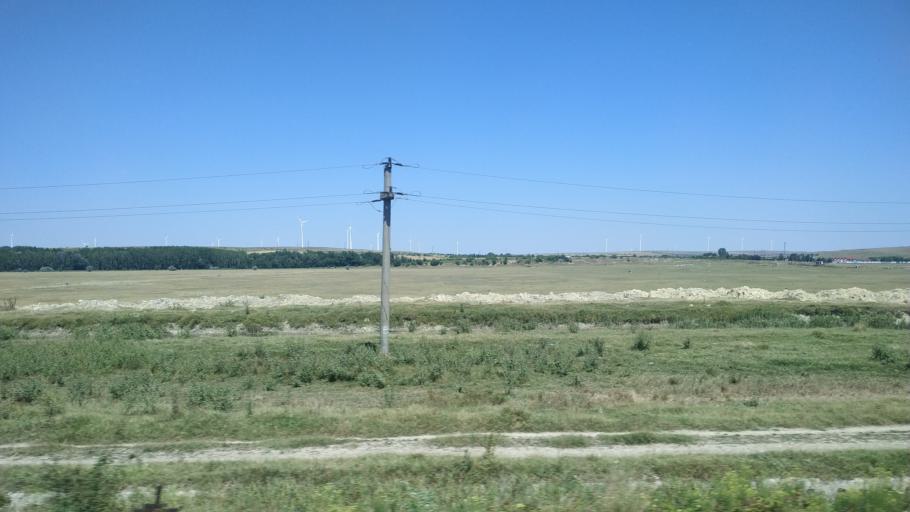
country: RO
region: Constanta
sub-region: Comuna Mircea Voda
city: Mircea Voda
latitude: 44.2642
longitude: 28.1649
